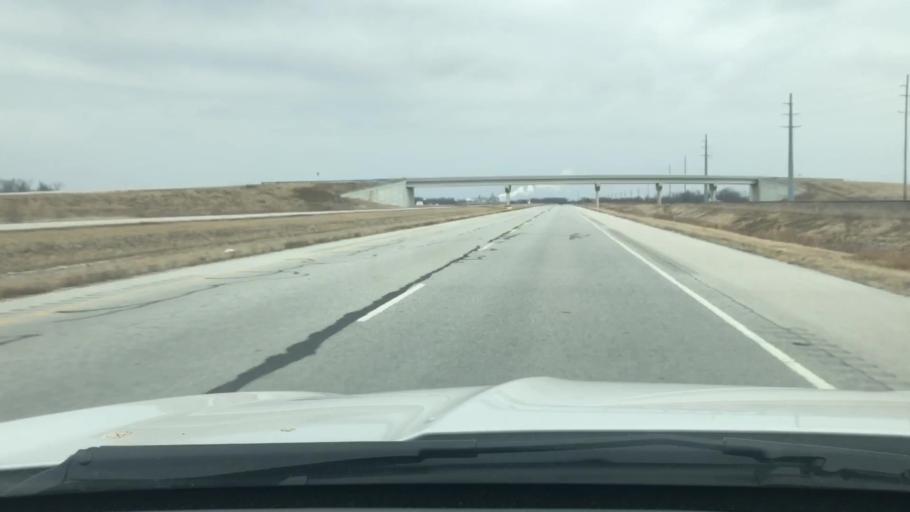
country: US
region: Indiana
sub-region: Cass County
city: Georgetown
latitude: 40.6913
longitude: -86.4801
